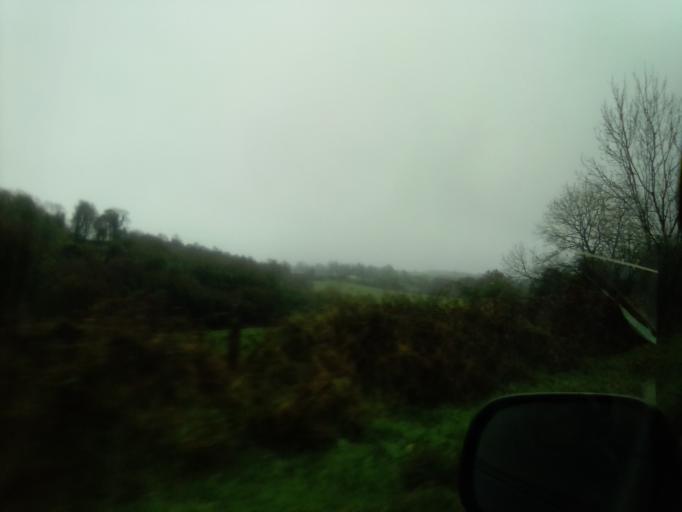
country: GB
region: Northern Ireland
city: Newtownstewart
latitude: 54.6943
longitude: -7.3539
